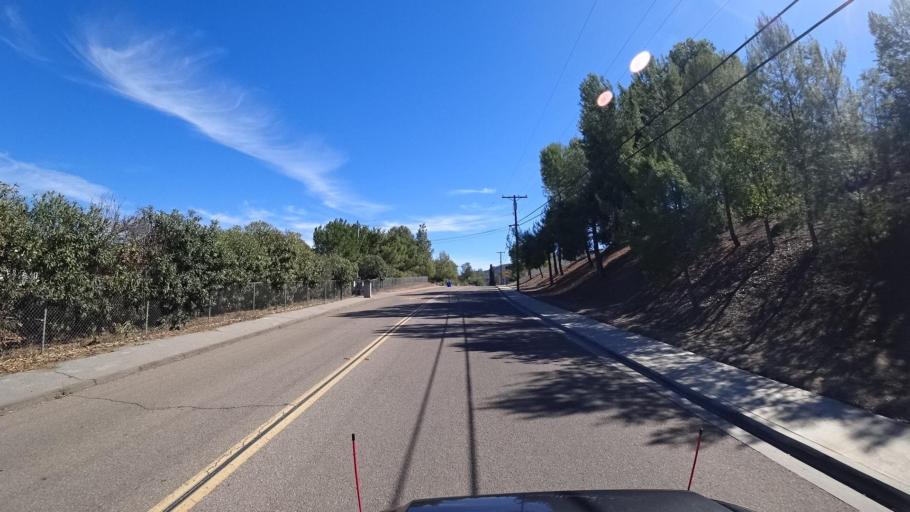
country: US
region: California
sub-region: San Diego County
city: Harbison Canyon
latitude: 32.8627
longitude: -116.8457
